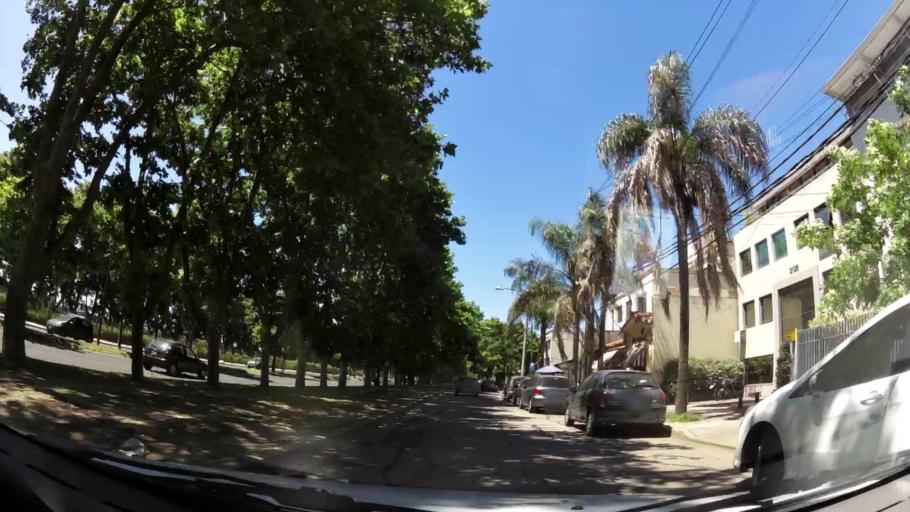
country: AR
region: Buenos Aires
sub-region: Partido de San Isidro
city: San Isidro
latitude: -34.4972
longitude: -58.5390
